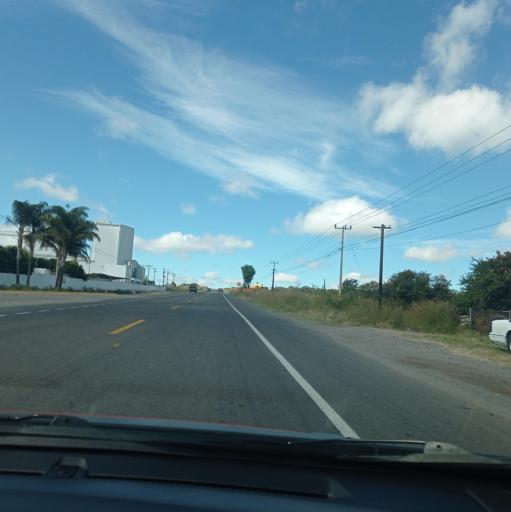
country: MX
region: Jalisco
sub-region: San Julian
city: Colonia Veintitres de Mayo
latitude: 21.0118
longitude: -102.2156
